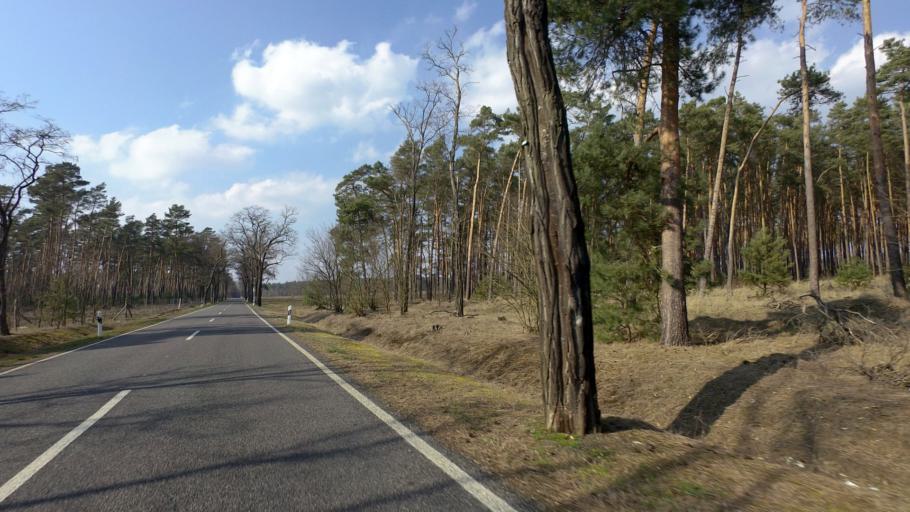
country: DE
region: Brandenburg
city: Dahme
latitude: 51.9211
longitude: 13.4761
